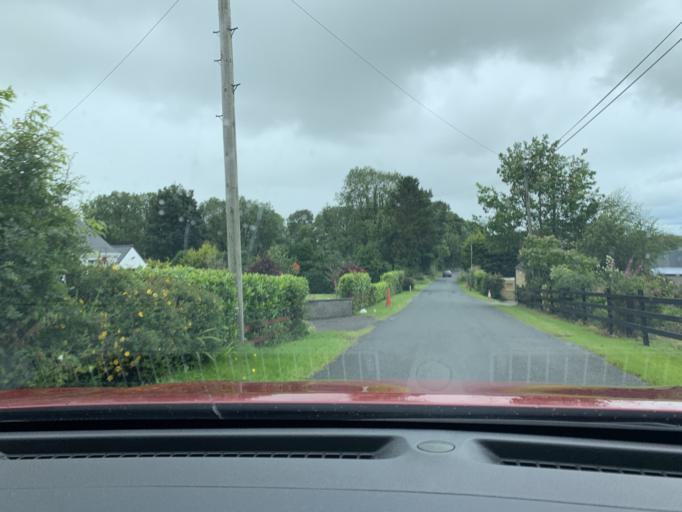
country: IE
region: Connaught
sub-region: County Leitrim
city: Carrick-on-Shannon
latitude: 53.8656
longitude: -8.1357
